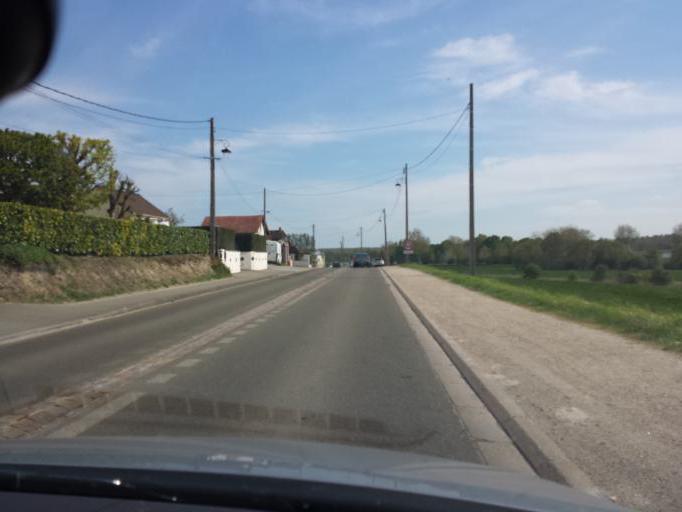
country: FR
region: Ile-de-France
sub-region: Departement des Yvelines
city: Villiers-Saint-Frederic
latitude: 48.8123
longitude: 1.8775
